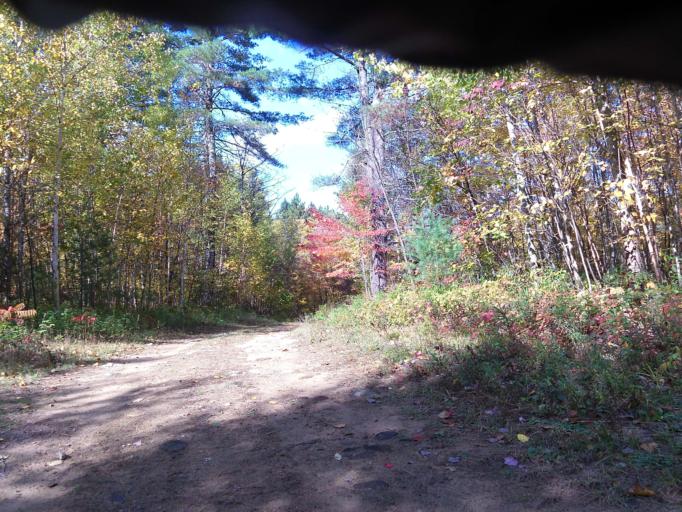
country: CA
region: Ontario
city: Petawawa
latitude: 45.8061
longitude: -77.2936
